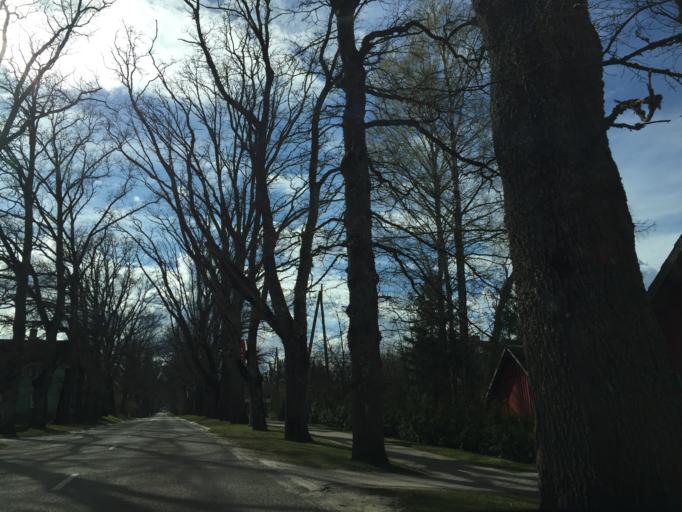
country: LV
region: Burtnieki
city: Matisi
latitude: 57.5973
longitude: 25.0897
